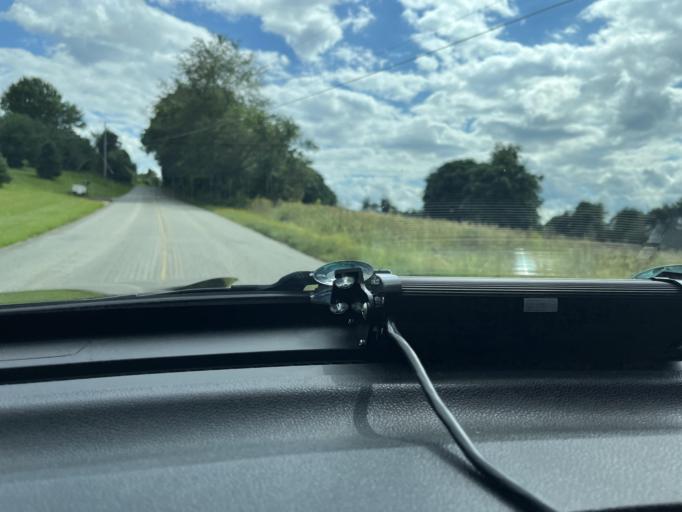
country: US
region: Pennsylvania
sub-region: Fayette County
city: South Uniontown
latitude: 39.9061
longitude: -79.7697
